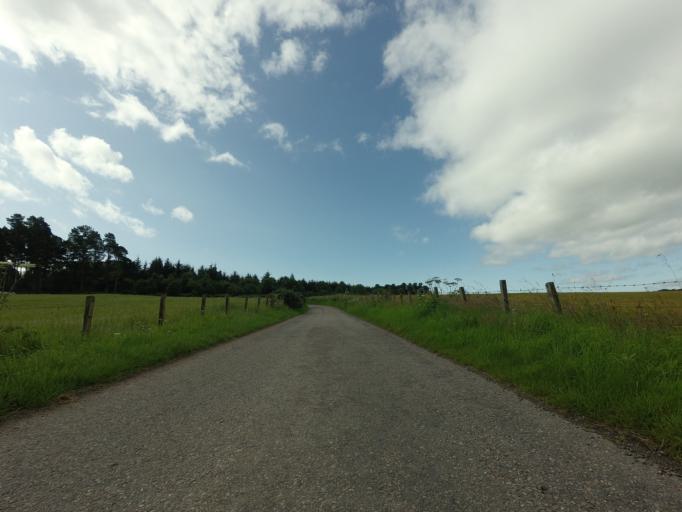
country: GB
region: Scotland
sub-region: Highland
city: Nairn
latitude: 57.5603
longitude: -3.8676
